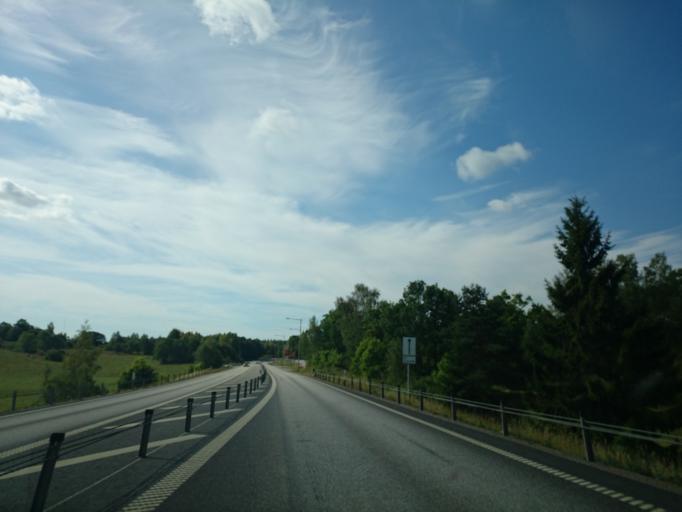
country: SE
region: Kalmar
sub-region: Vasterviks Kommun
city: Forserum
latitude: 57.9817
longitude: 16.4827
